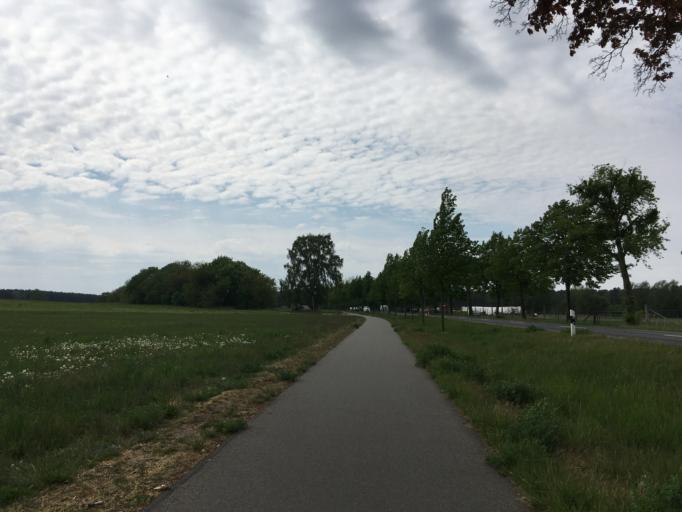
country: DE
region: Brandenburg
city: Rudnitz
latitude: 52.7184
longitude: 13.6224
